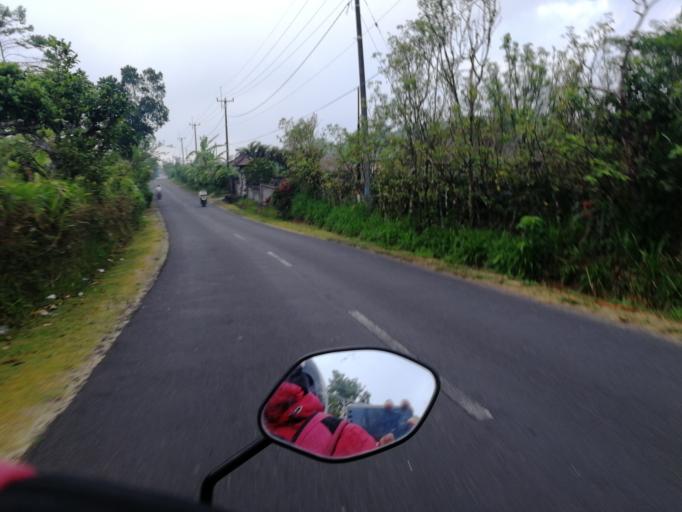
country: ID
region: Bali
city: Banjar Ambengan
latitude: -8.2341
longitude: 115.2413
